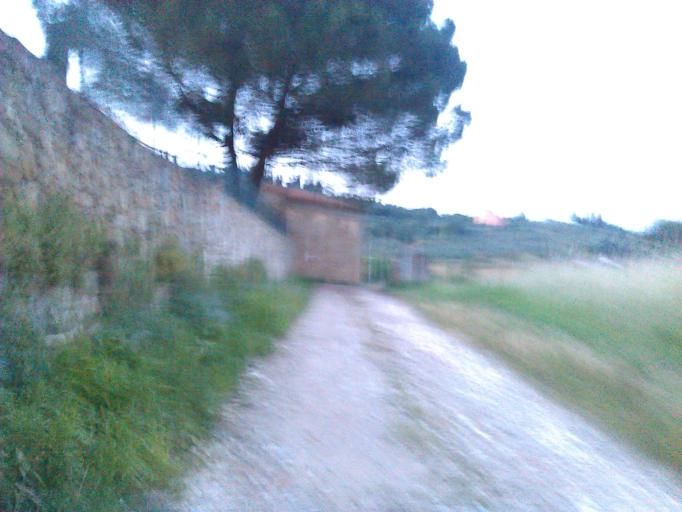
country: IT
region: Tuscany
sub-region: Province of Arezzo
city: Viciomaggio
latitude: 43.4438
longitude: 11.7746
